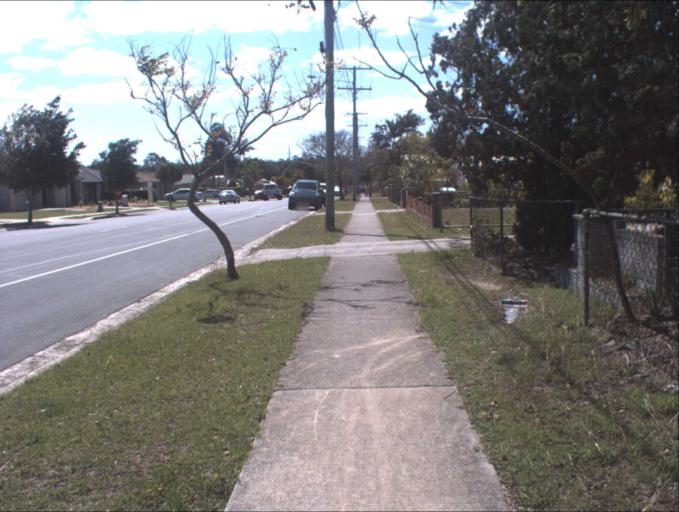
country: AU
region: Queensland
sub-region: Logan
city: Logan City
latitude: -27.6724
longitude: 153.1016
